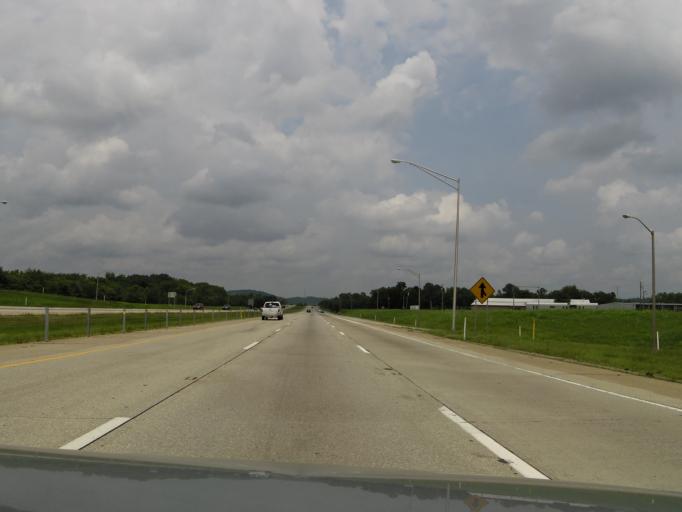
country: US
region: Kentucky
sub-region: Bullitt County
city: Shepherdsville
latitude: 37.9269
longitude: -85.6876
